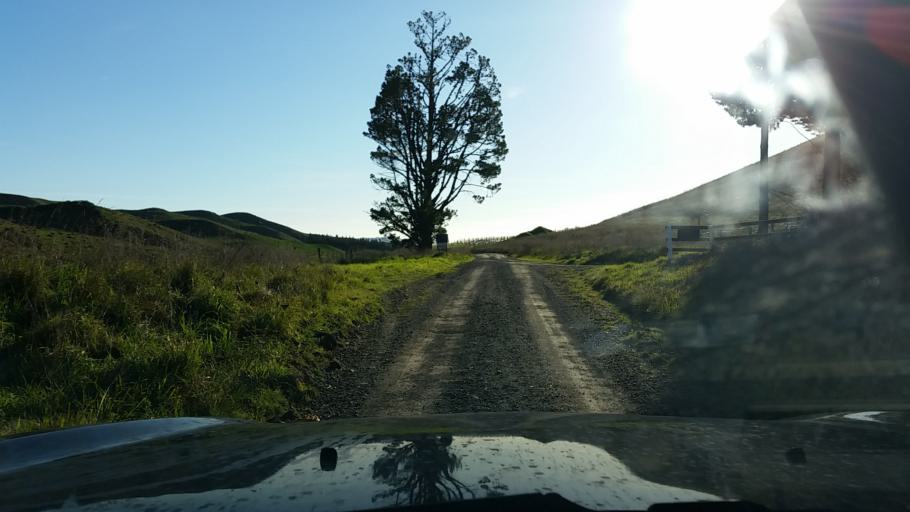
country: NZ
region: Marlborough
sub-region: Marlborough District
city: Blenheim
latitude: -41.7331
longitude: 174.0021
